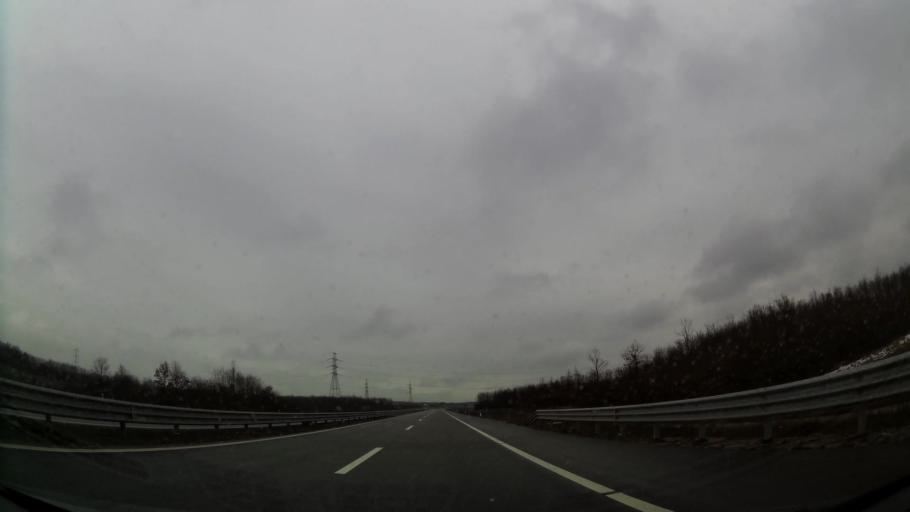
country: XK
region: Ferizaj
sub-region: Komuna e Ferizajt
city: Ferizaj
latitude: 42.3790
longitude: 21.2042
